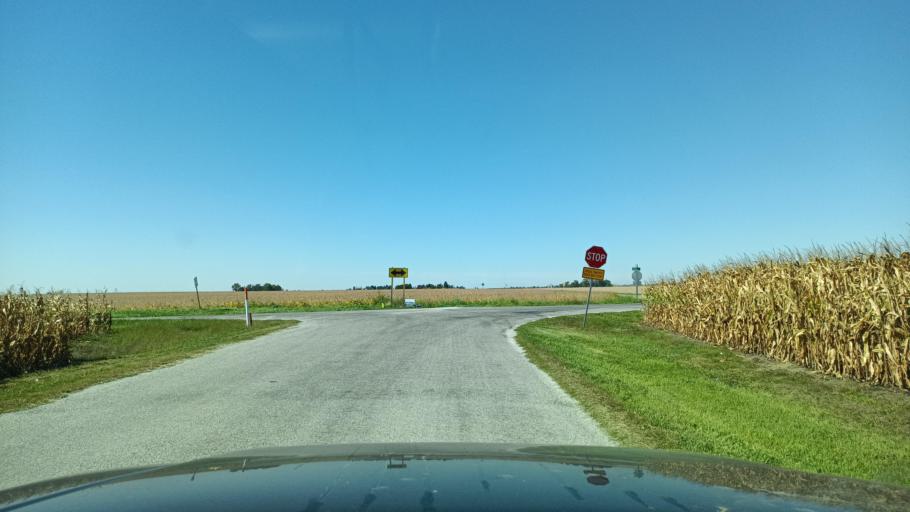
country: US
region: Illinois
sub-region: Champaign County
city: Savoy
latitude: 40.0986
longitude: -88.3501
